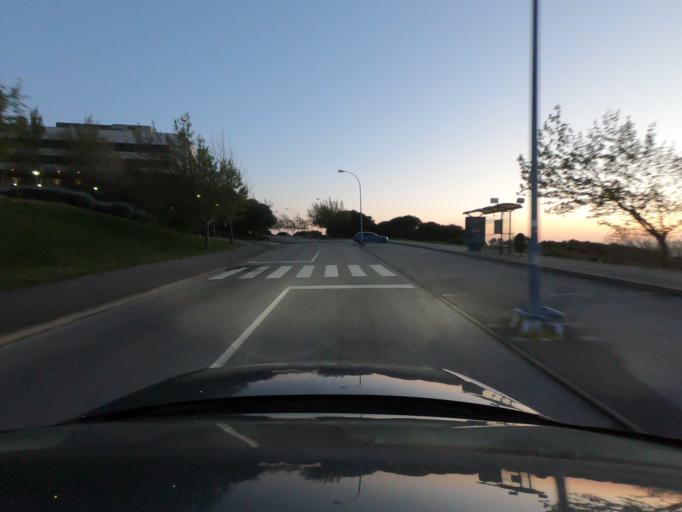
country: PT
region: Lisbon
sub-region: Oeiras
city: Porto Salvo
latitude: 38.7416
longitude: -9.3052
